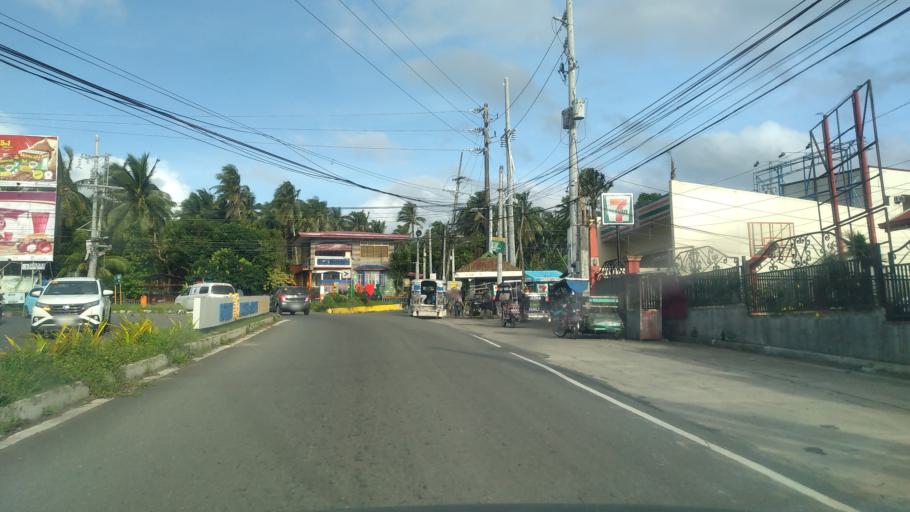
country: PH
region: Calabarzon
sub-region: Province of Quezon
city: Calumpang
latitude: 13.9756
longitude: 121.5572
